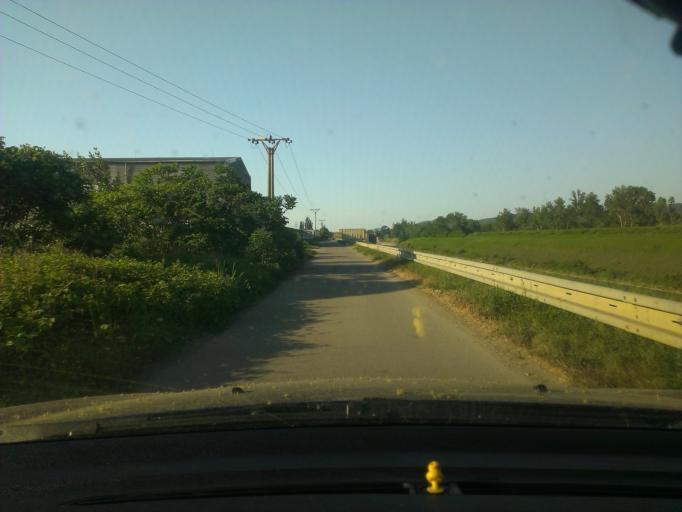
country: SK
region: Trnavsky
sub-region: Okres Trnava
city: Piestany
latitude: 48.6530
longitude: 17.8514
